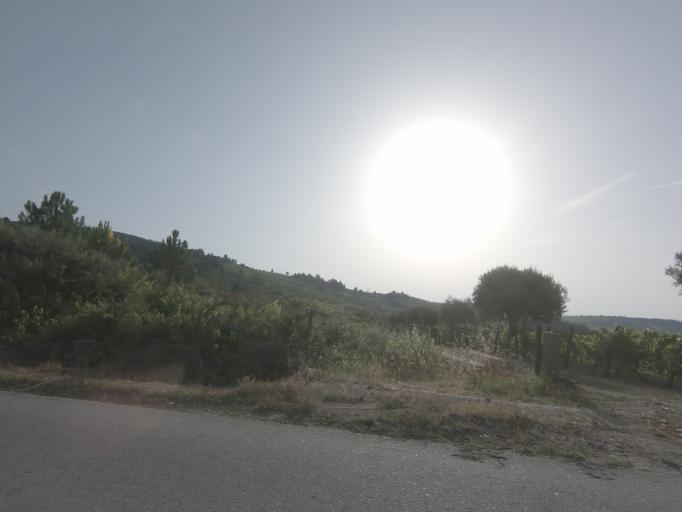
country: PT
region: Viseu
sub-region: Sao Joao da Pesqueira
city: Sao Joao da Pesqueira
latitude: 41.2423
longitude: -7.4651
